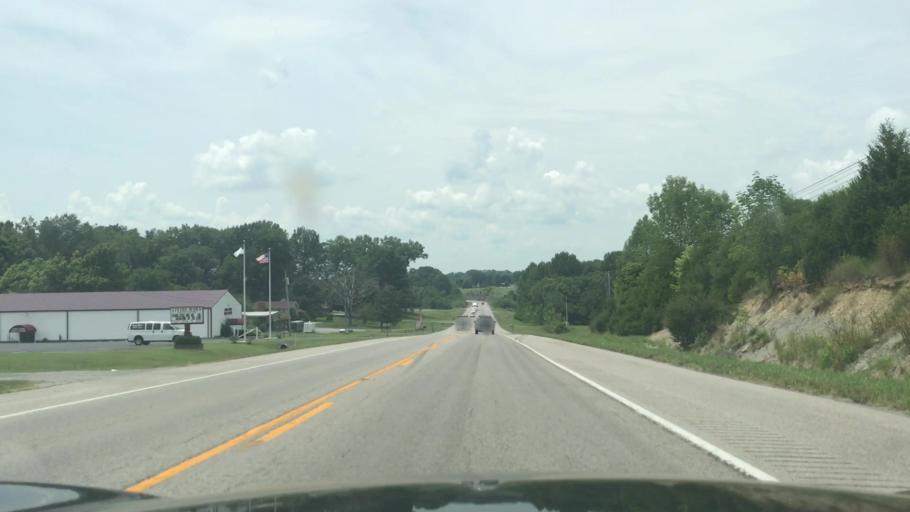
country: US
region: Kentucky
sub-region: Green County
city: Greensburg
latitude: 37.2872
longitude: -85.4813
